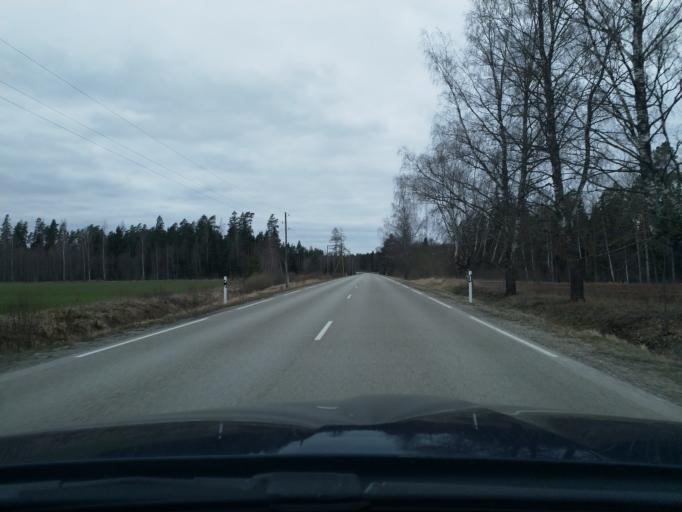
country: LV
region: Talsu Rajons
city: Sabile
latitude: 56.9524
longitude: 22.3038
